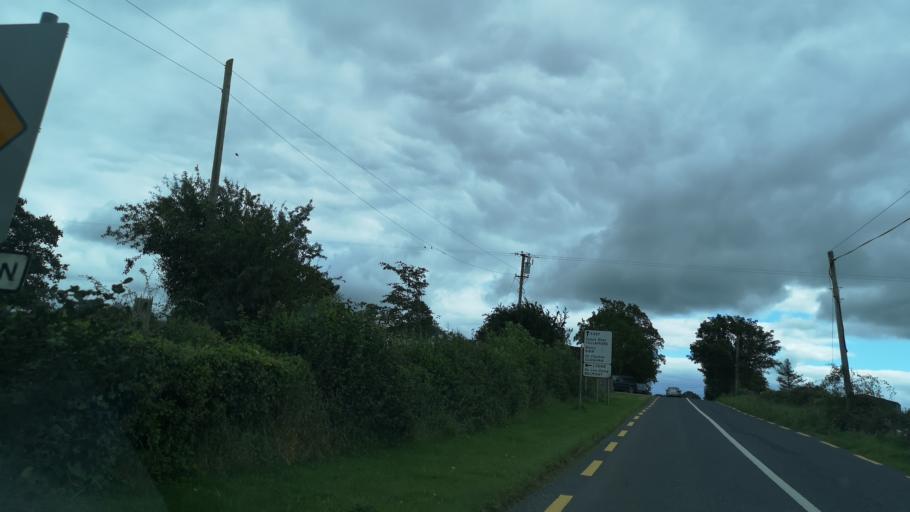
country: IE
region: Leinster
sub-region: Uibh Fhaili
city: Banagher
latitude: 53.2448
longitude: -7.9393
